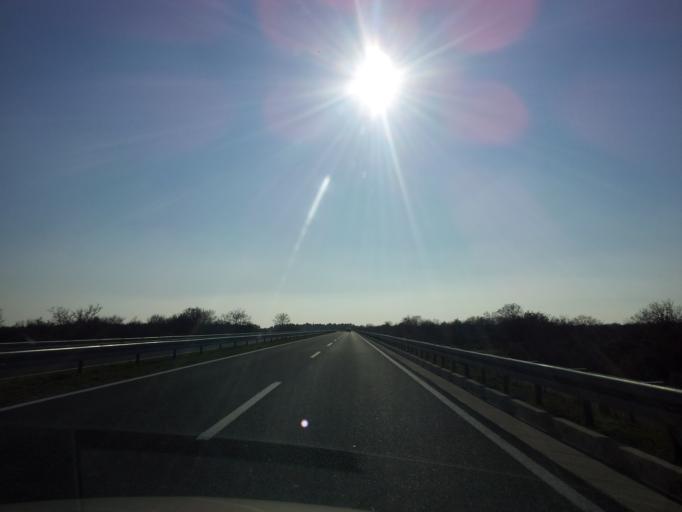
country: HR
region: Zadarska
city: Galovac
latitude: 44.0948
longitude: 15.3719
